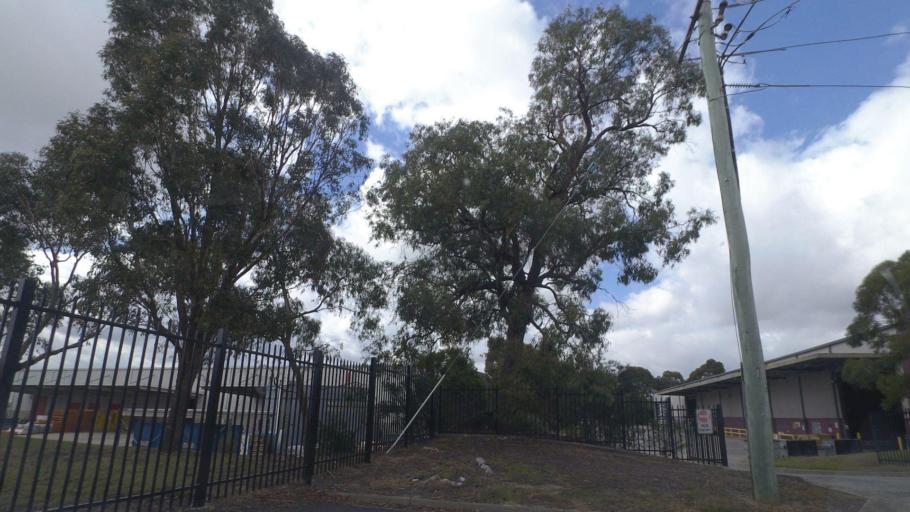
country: AU
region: Victoria
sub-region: Knox
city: Scoresby
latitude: -37.9043
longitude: 145.2313
